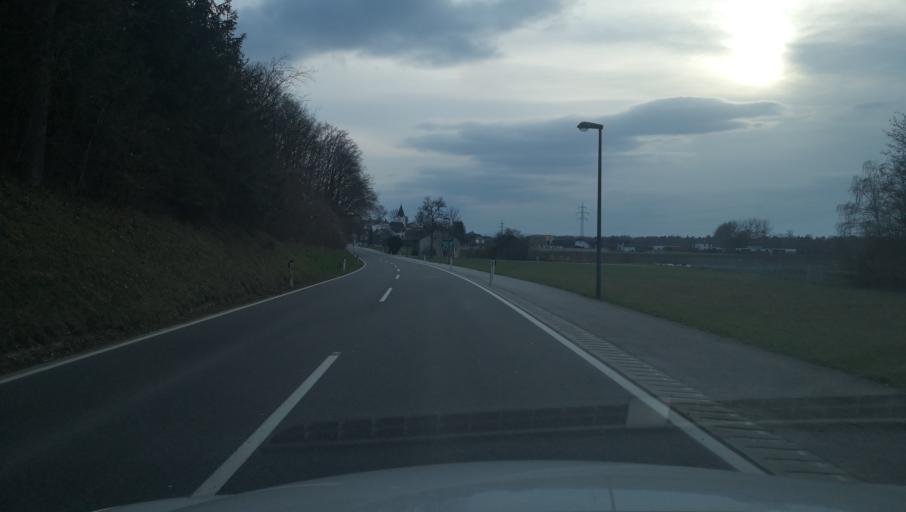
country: AT
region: Lower Austria
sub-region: Politischer Bezirk Amstetten
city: Winklarn
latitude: 48.0954
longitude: 14.8540
